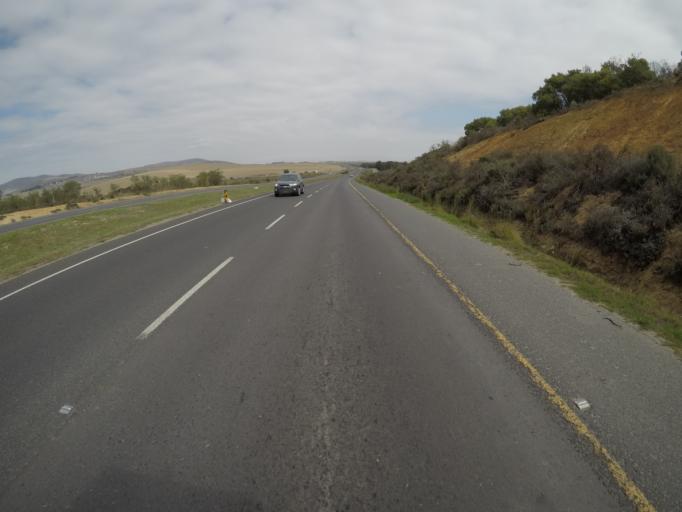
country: ZA
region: Western Cape
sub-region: City of Cape Town
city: Sunset Beach
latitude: -33.7861
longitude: 18.5490
